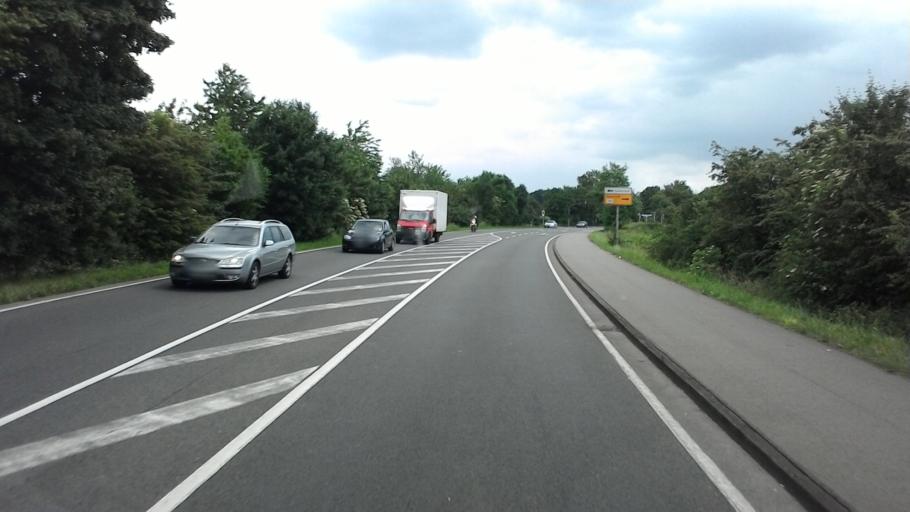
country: BE
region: Wallonia
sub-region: Province de Liege
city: Raeren
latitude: 50.6934
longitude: 6.1581
